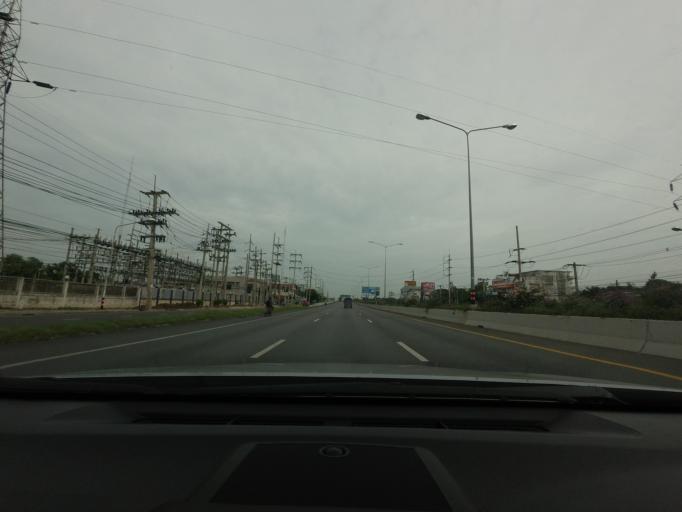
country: TH
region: Phetchaburi
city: Phetchaburi
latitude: 13.0898
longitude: 99.9417
